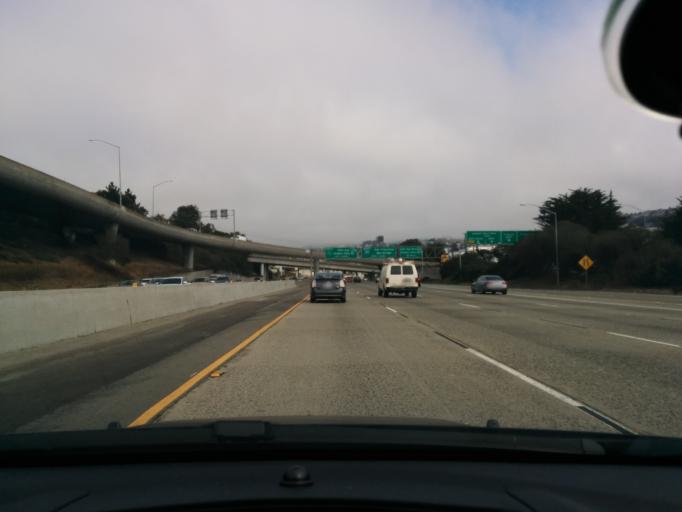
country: US
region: California
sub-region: San Mateo County
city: Broadmoor
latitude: 37.6819
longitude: -122.4715
